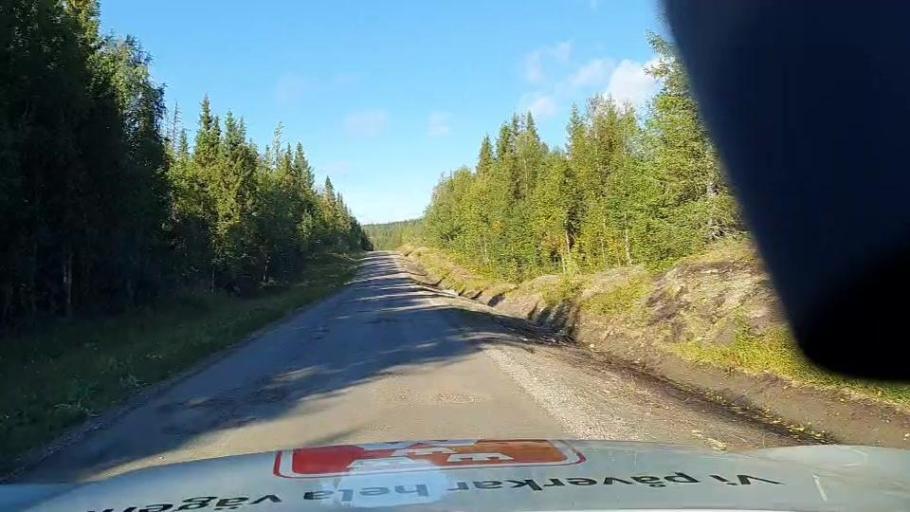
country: SE
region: Jaemtland
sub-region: Stroemsunds Kommun
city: Stroemsund
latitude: 64.5523
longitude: 15.0905
